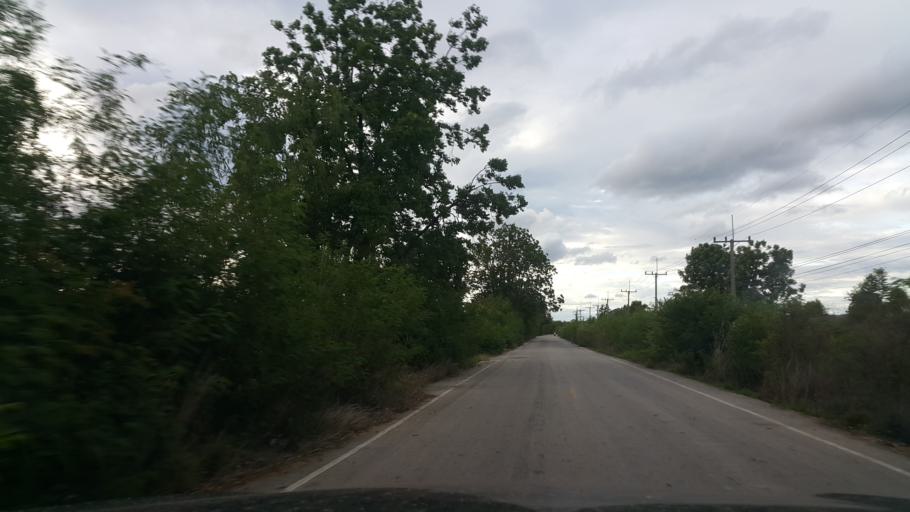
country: TH
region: Sukhothai
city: Thung Saliam
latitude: 17.1631
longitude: 99.5239
